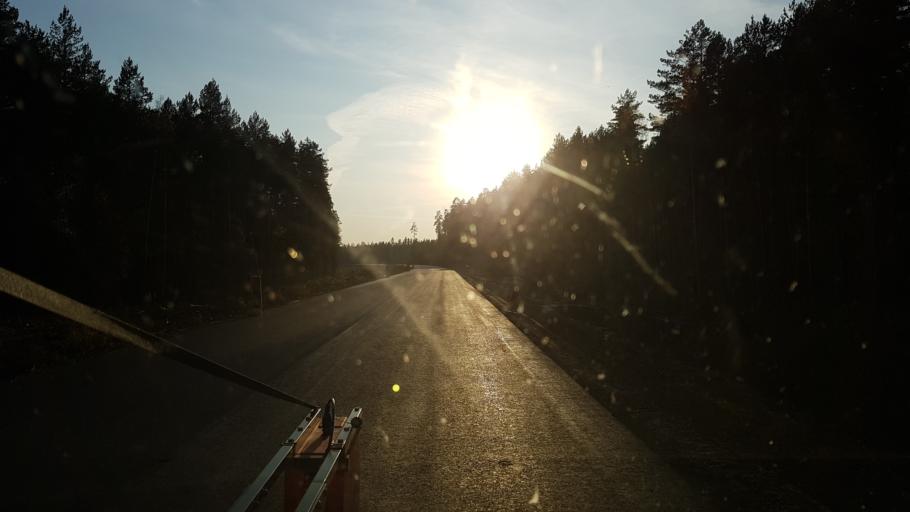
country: EE
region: Polvamaa
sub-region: Polva linn
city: Polva
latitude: 57.9372
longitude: 27.1937
